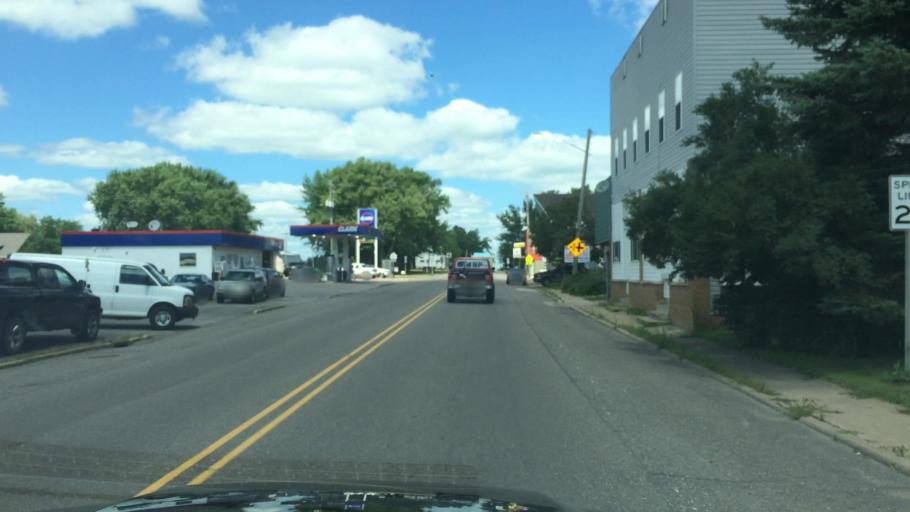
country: US
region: Wisconsin
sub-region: Taylor County
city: Medford
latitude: 45.0758
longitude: -90.3148
